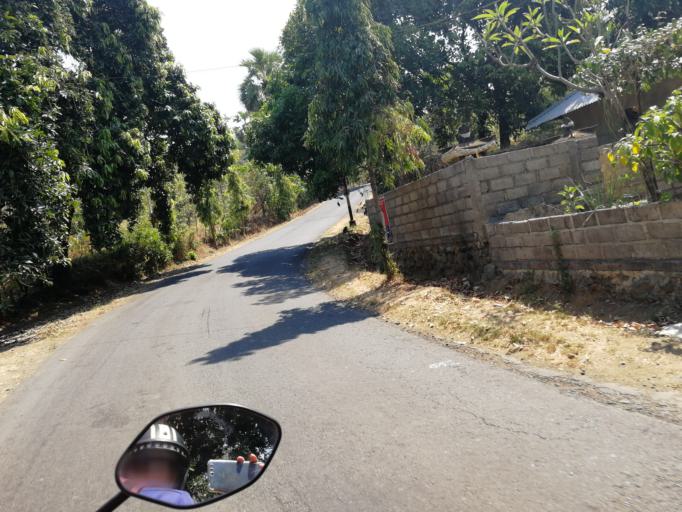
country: ID
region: Bali
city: Banjar Trunyan
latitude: -8.1266
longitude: 115.3279
